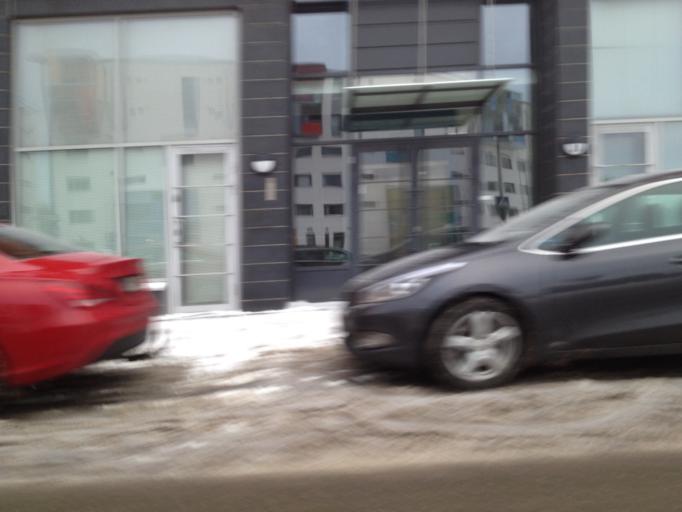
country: FI
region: Uusimaa
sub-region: Helsinki
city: Vantaa
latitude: 60.2075
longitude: 25.1578
